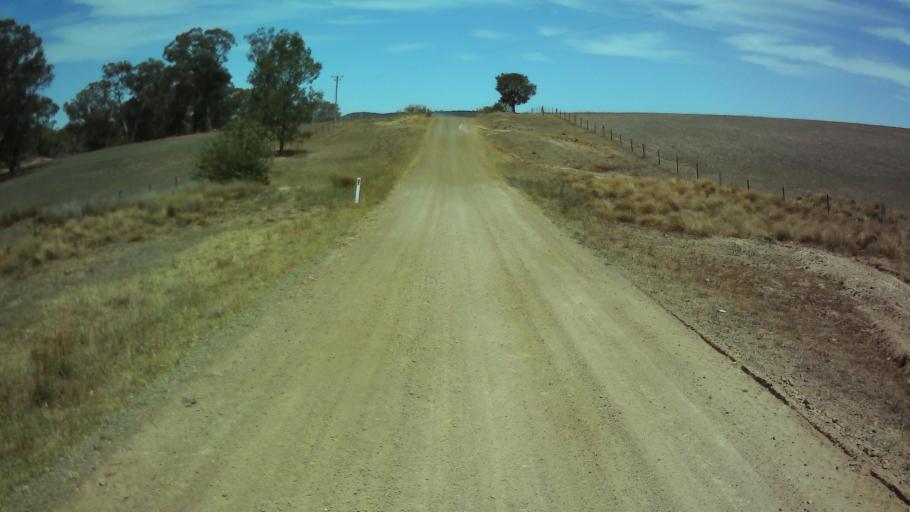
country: AU
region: New South Wales
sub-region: Weddin
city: Grenfell
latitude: -33.8218
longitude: 148.1683
